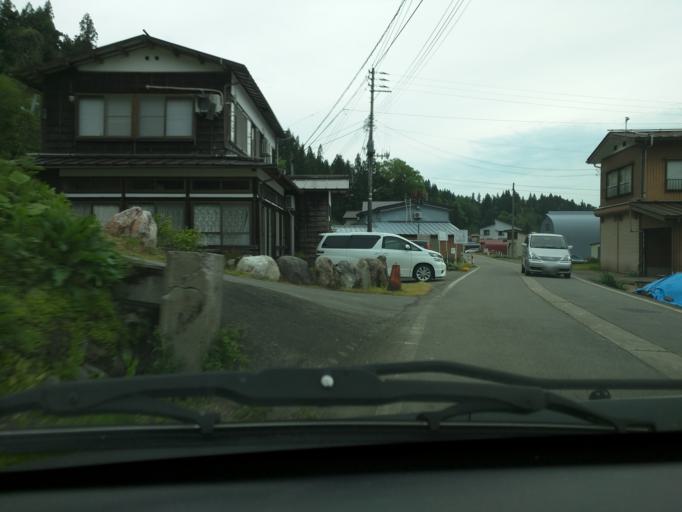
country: JP
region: Niigata
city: Muikamachi
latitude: 37.2166
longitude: 138.9498
